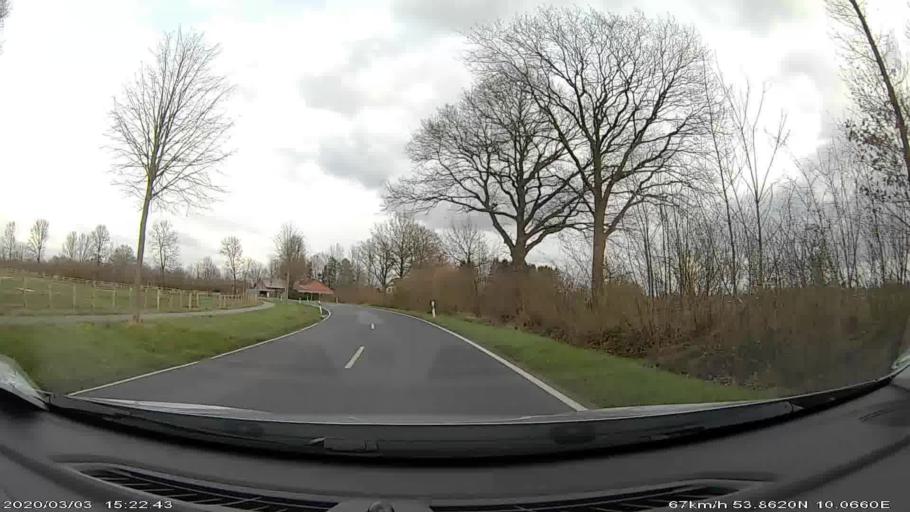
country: DE
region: Schleswig-Holstein
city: Struvenhutten
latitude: 53.8624
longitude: 10.0651
